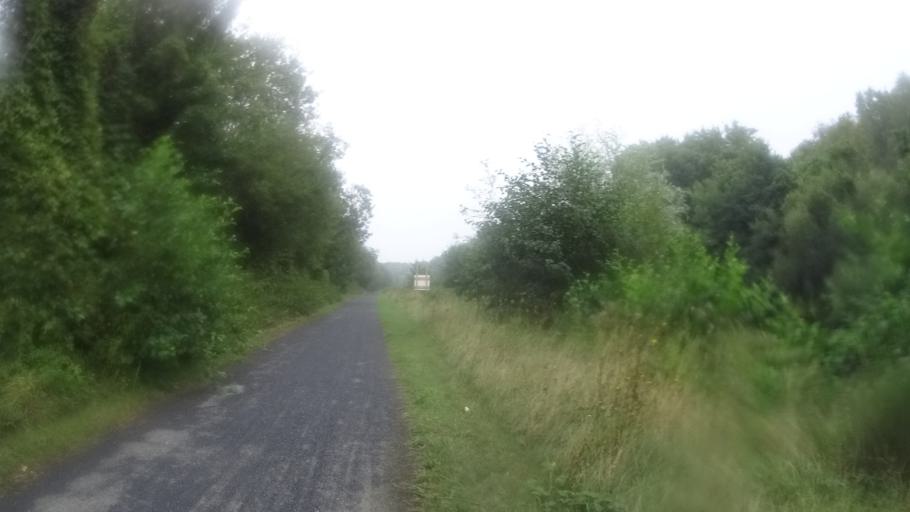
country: FR
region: Nord-Pas-de-Calais
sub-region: Departement du Nord
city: Hautmont
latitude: 50.2625
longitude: 3.9360
